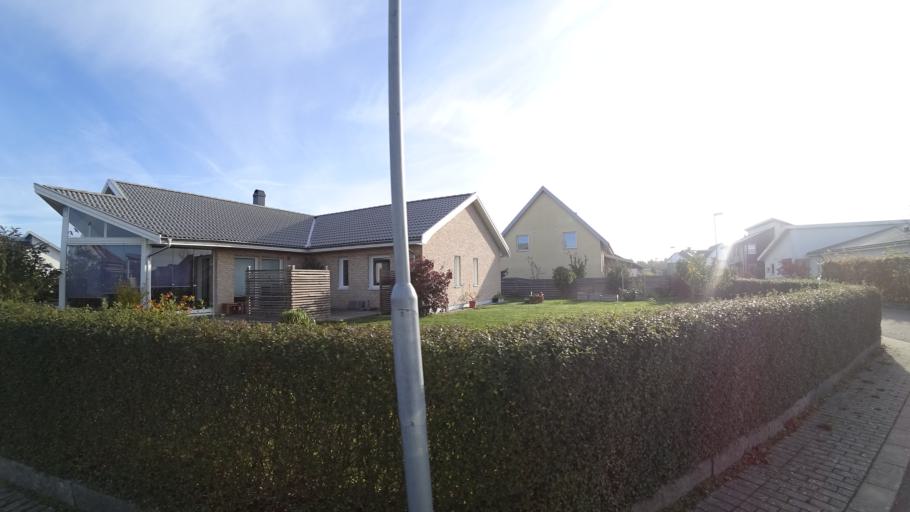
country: SE
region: Skane
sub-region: Staffanstorps Kommun
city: Staffanstorp
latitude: 55.6348
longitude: 13.2221
